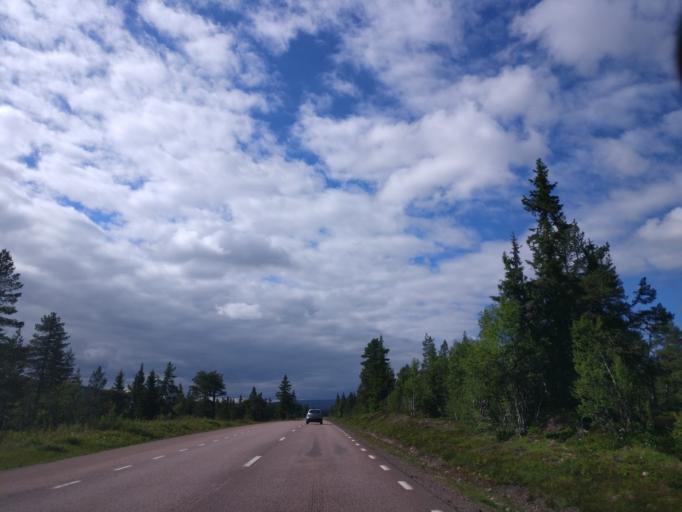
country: SE
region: Dalarna
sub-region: Malung-Saelens kommun
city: Malung
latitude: 61.1664
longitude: 13.0978
